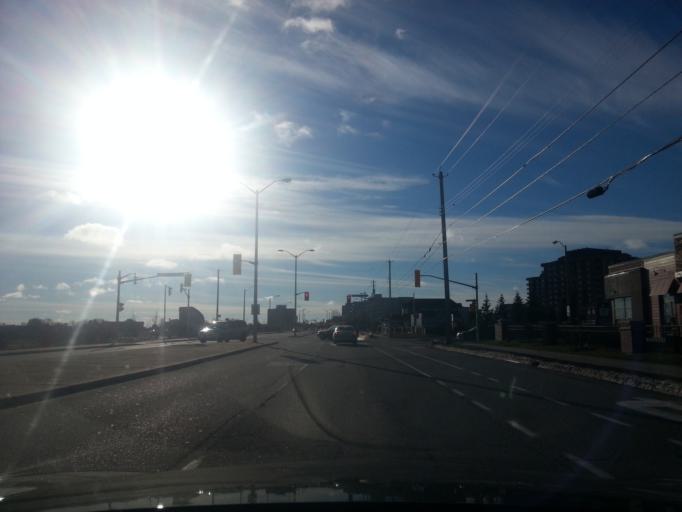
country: CA
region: Ontario
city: Ottawa
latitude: 45.3708
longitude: -75.7322
